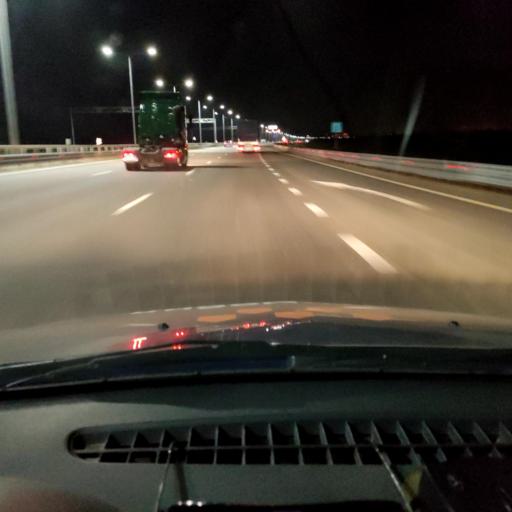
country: RU
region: Voronezj
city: Somovo
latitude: 51.7765
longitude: 39.2988
